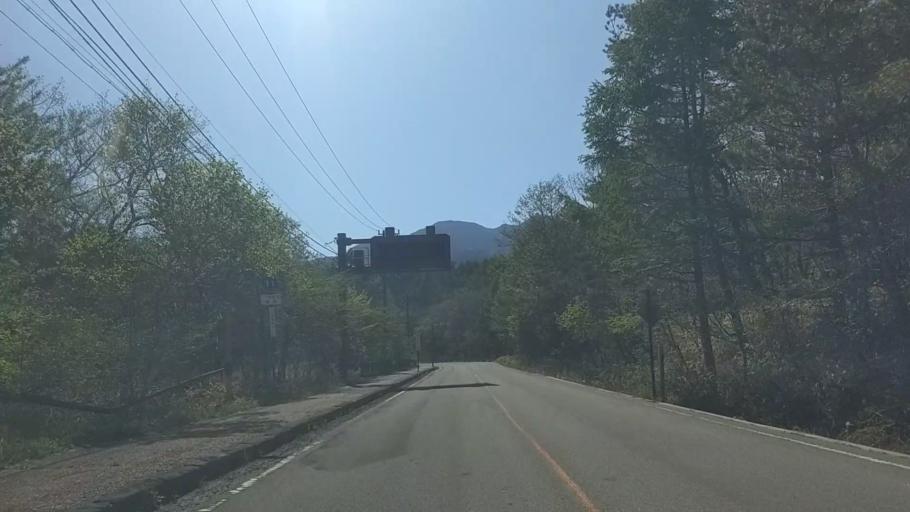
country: JP
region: Yamanashi
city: Nirasaki
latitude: 35.9351
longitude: 138.4238
